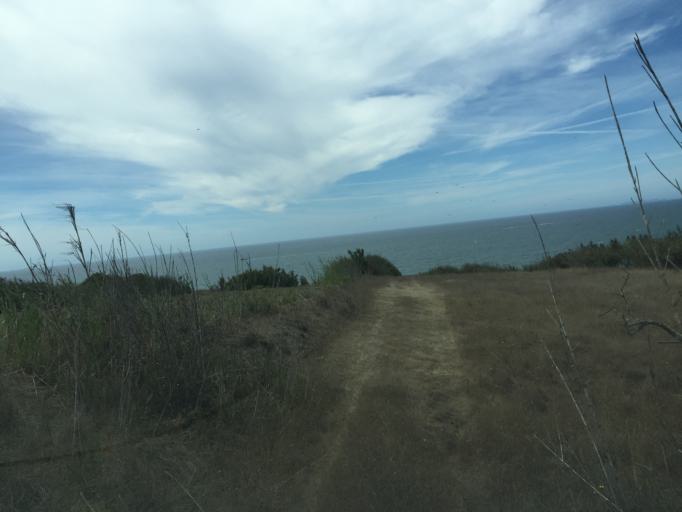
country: PT
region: Lisbon
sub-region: Lourinha
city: Lourinha
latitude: 39.1997
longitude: -9.3455
